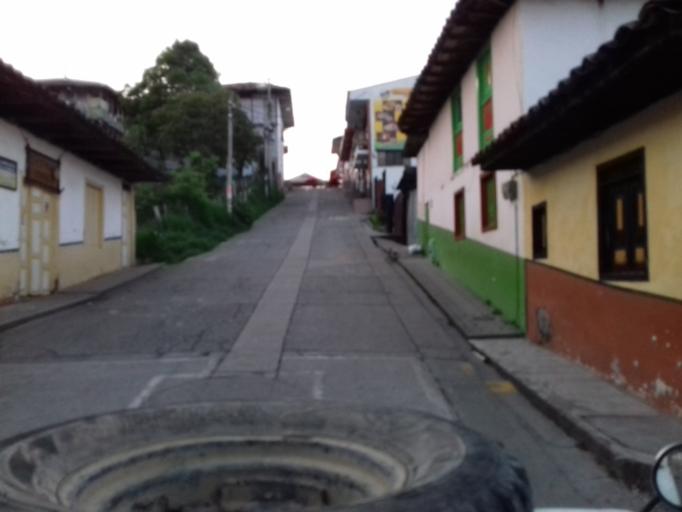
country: CO
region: Quindio
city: Salento
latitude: 4.6380
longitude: -75.5707
